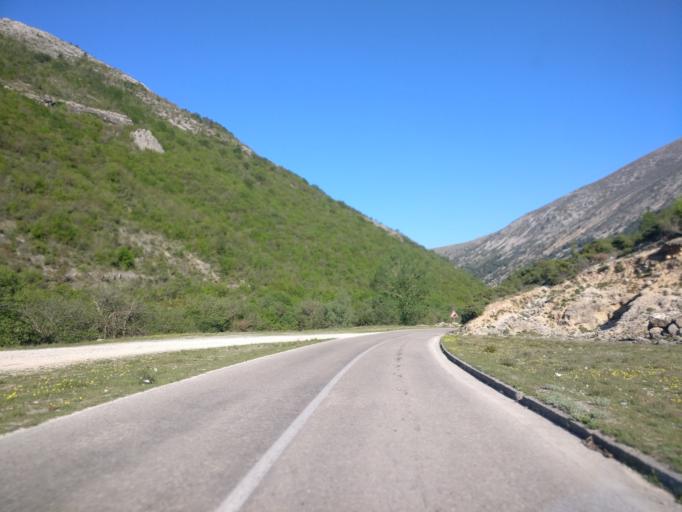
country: BA
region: Federation of Bosnia and Herzegovina
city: Stolac
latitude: 43.0915
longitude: 17.9965
